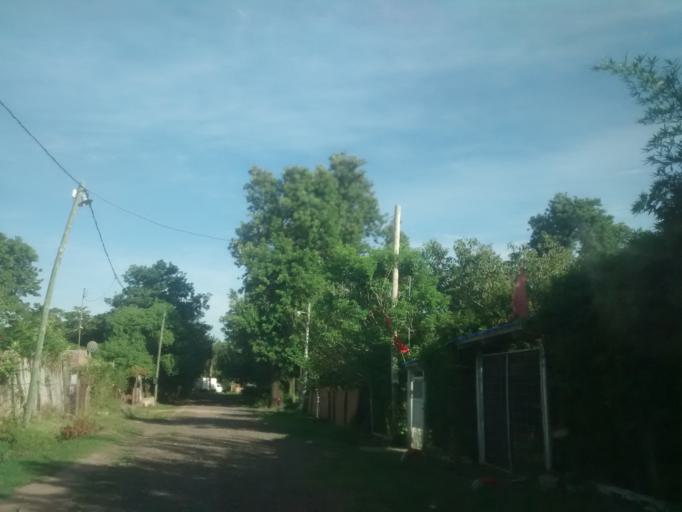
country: AR
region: Chaco
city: Puerto Tirol
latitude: -27.3771
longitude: -59.0937
